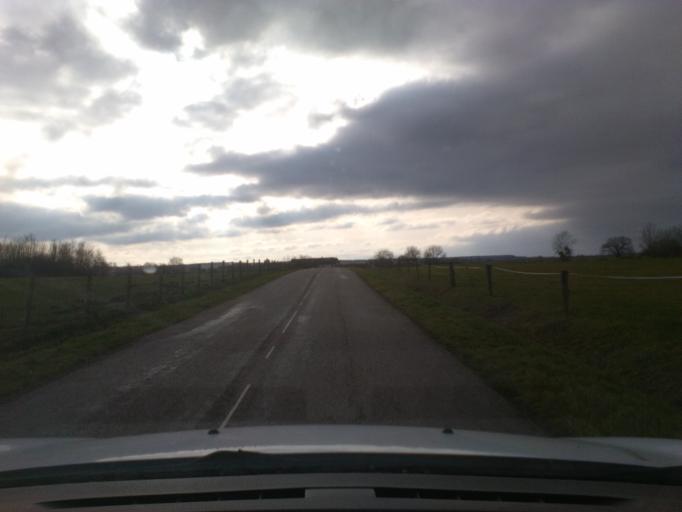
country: FR
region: Lorraine
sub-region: Departement des Vosges
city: Vittel
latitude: 48.3312
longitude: 5.9867
